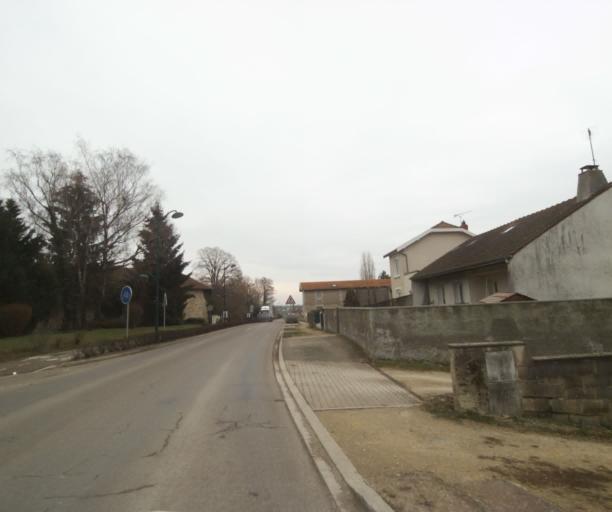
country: FR
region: Champagne-Ardenne
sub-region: Departement de la Haute-Marne
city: Villiers-en-Lieu
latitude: 48.6650
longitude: 4.9051
